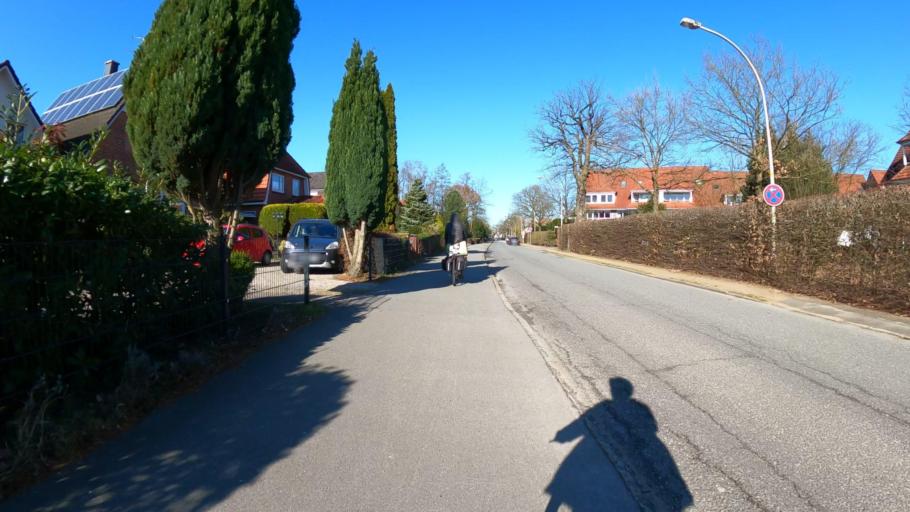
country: DE
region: Schleswig-Holstein
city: Rellingen
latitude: 53.6419
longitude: 9.8005
